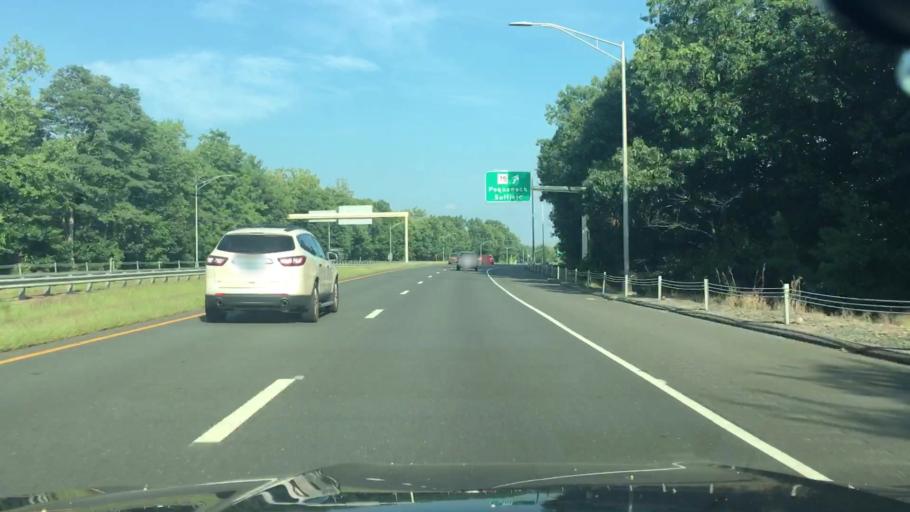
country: US
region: Connecticut
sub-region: Hartford County
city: Windsor Locks
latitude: 41.9175
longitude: -72.6809
